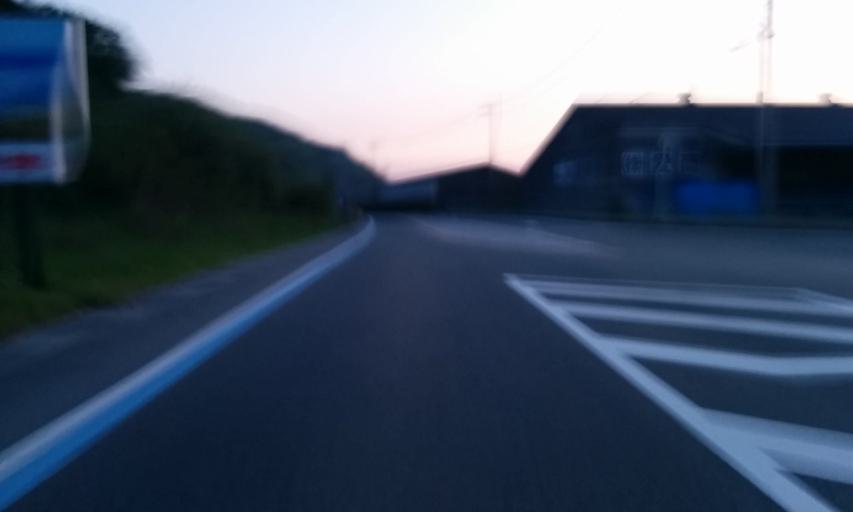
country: JP
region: Ehime
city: Ozu
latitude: 33.6197
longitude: 132.4972
